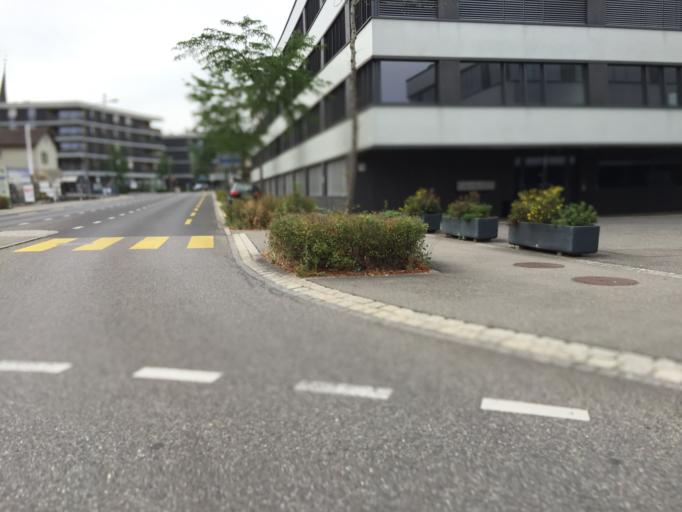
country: CH
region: Bern
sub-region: Bern-Mittelland District
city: Koniz
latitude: 46.9239
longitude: 7.4130
